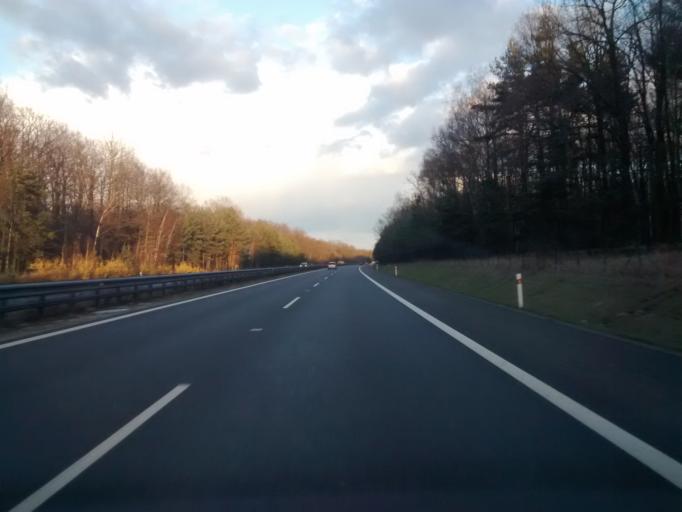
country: CZ
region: Central Bohemia
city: Poricany
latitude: 50.1267
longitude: 14.9124
